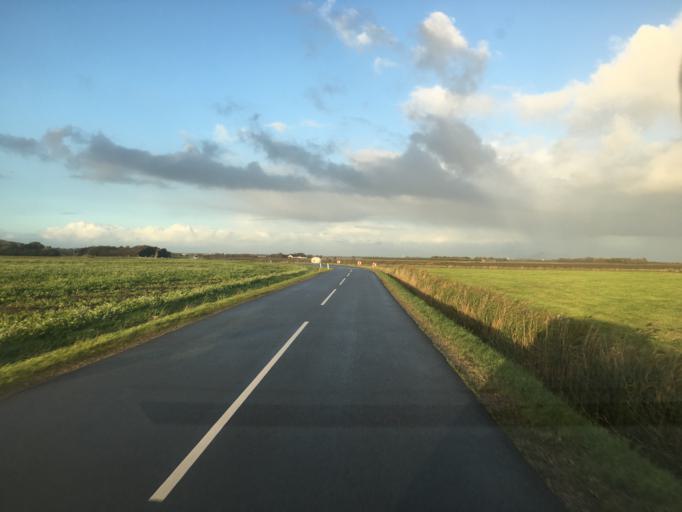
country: DE
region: Schleswig-Holstein
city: Aventoft
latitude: 54.9153
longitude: 8.7815
